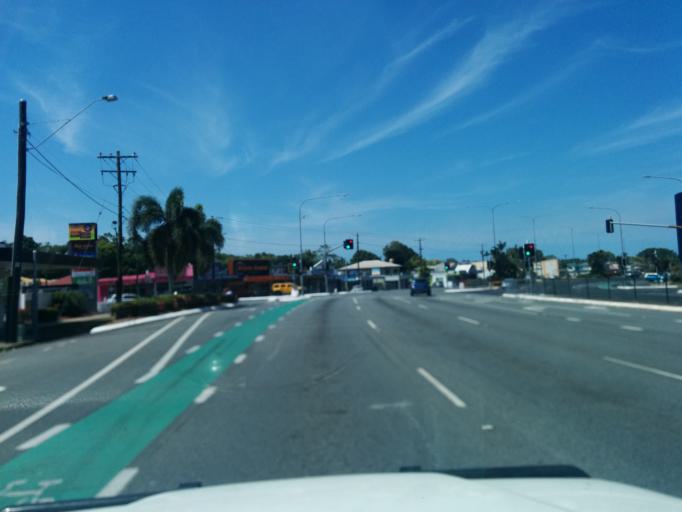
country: AU
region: Queensland
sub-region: Cairns
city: Woree
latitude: -16.9434
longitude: 145.7385
